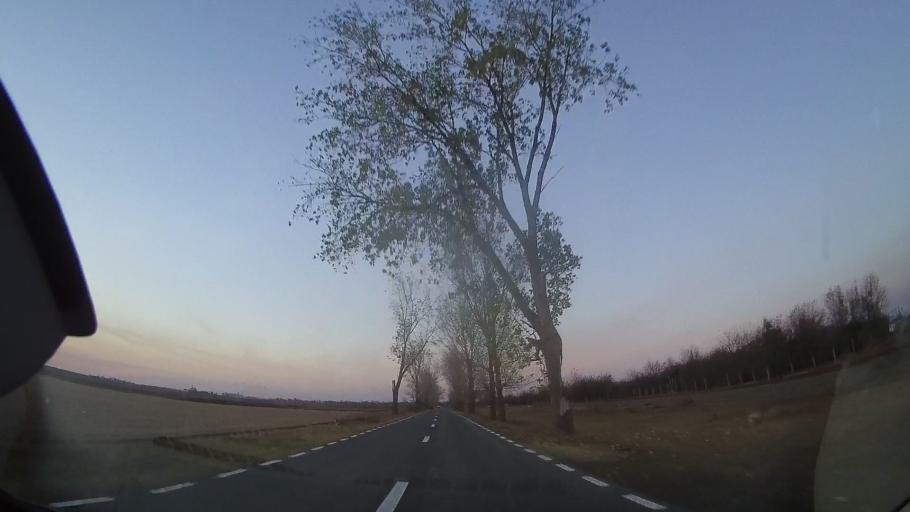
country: RO
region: Constanta
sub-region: Comuna Cobadin
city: Cobadin
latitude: 44.0442
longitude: 28.2540
